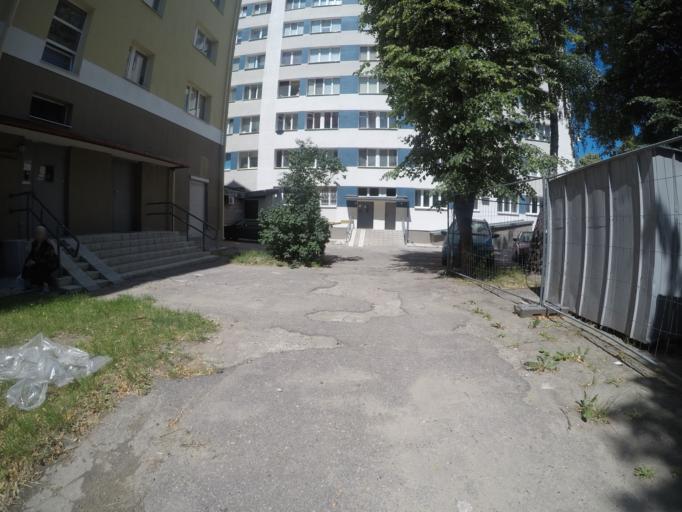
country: BY
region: Grodnenskaya
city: Hrodna
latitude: 53.6986
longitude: 23.8205
